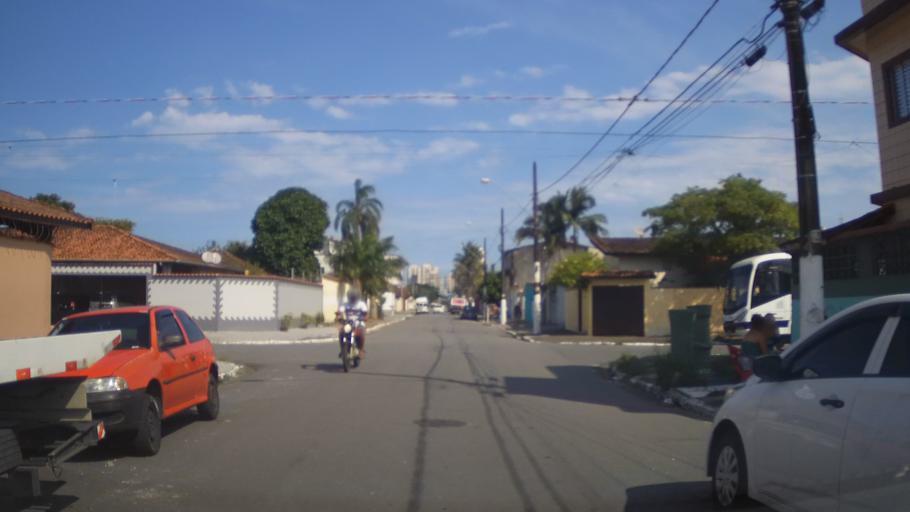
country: BR
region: Sao Paulo
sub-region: Praia Grande
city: Praia Grande
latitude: -23.9968
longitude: -46.4198
